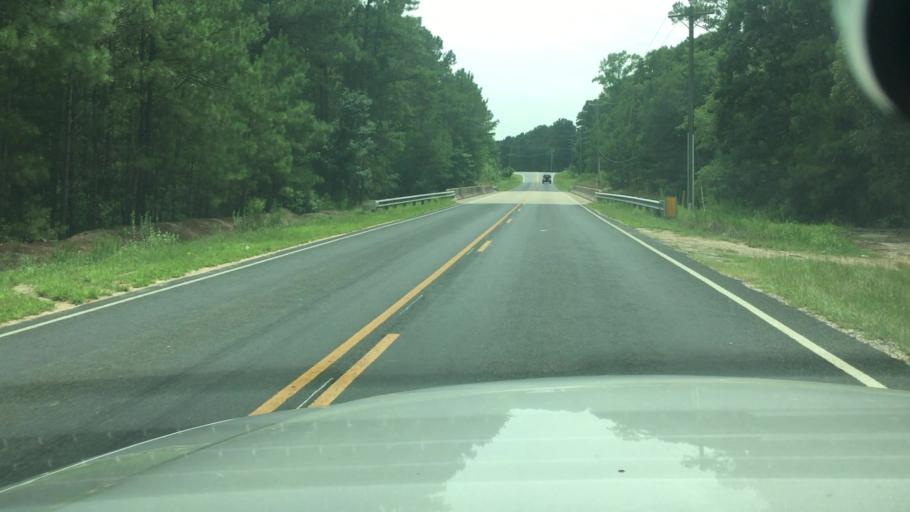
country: US
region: North Carolina
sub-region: Cumberland County
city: Hope Mills
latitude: 34.9616
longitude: -78.8992
